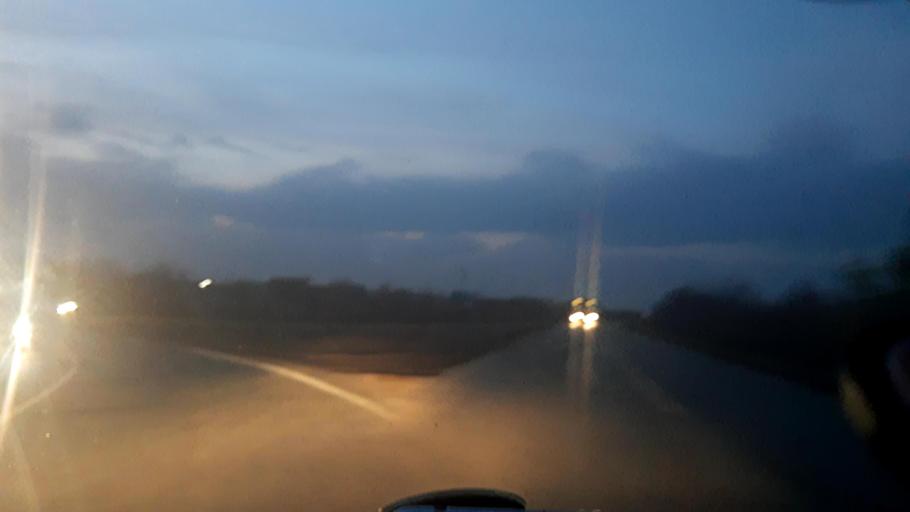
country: RU
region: Bashkortostan
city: Iglino
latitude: 54.7757
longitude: 56.2556
